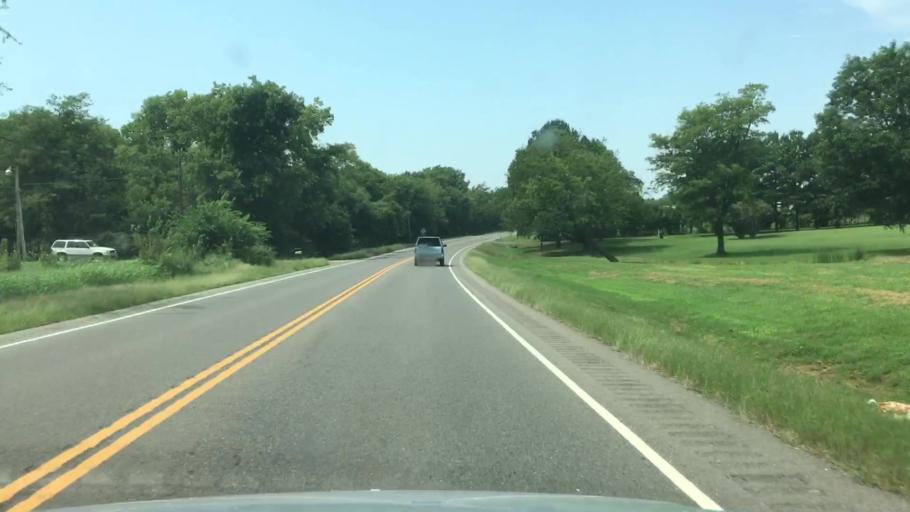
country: US
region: Oklahoma
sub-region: Wagoner County
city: Wagoner
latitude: 35.9373
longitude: -95.3155
